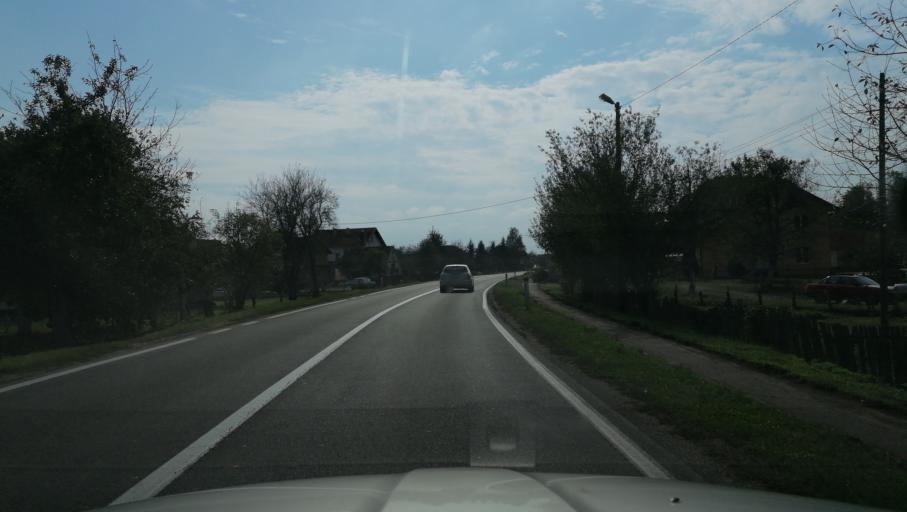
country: BA
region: Republika Srpska
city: Balatun
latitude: 44.8689
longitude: 19.3310
